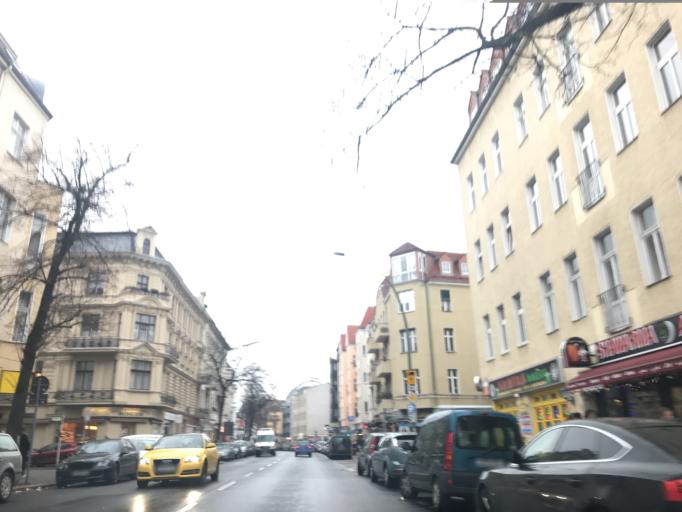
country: DE
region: Berlin
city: Wilhelmstadt
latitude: 52.5231
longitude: 13.1977
